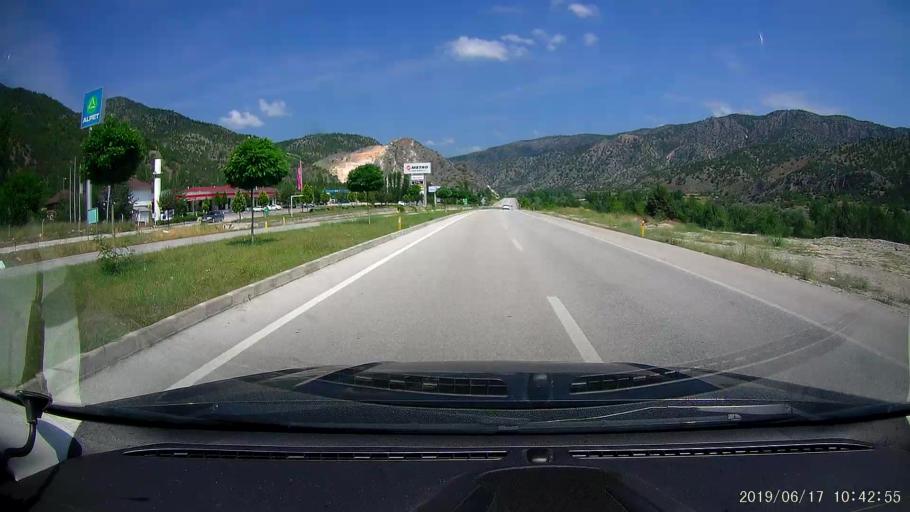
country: TR
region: Corum
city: Kargi
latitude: 41.0547
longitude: 34.5449
